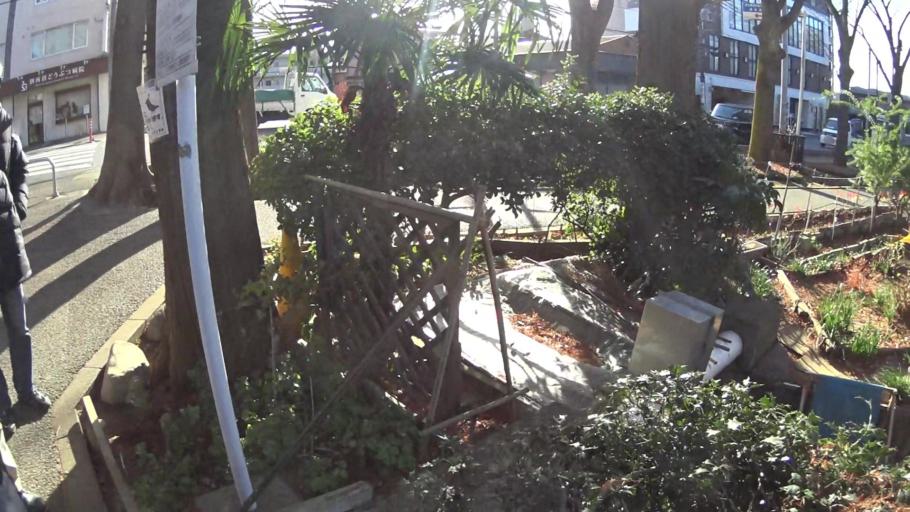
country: JP
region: Saitama
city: Yono
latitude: 35.8550
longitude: 139.6439
